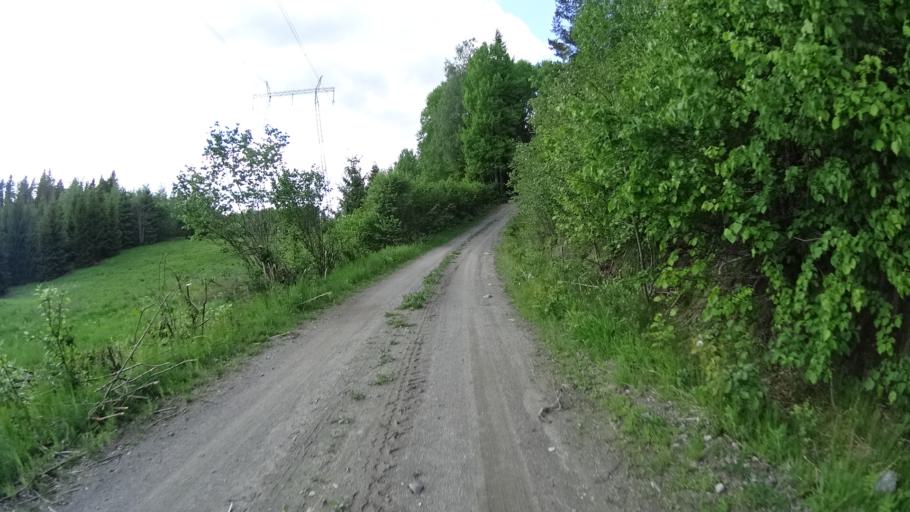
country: FI
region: Uusimaa
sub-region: Raaseporin
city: Karis
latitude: 60.1517
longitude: 23.6244
